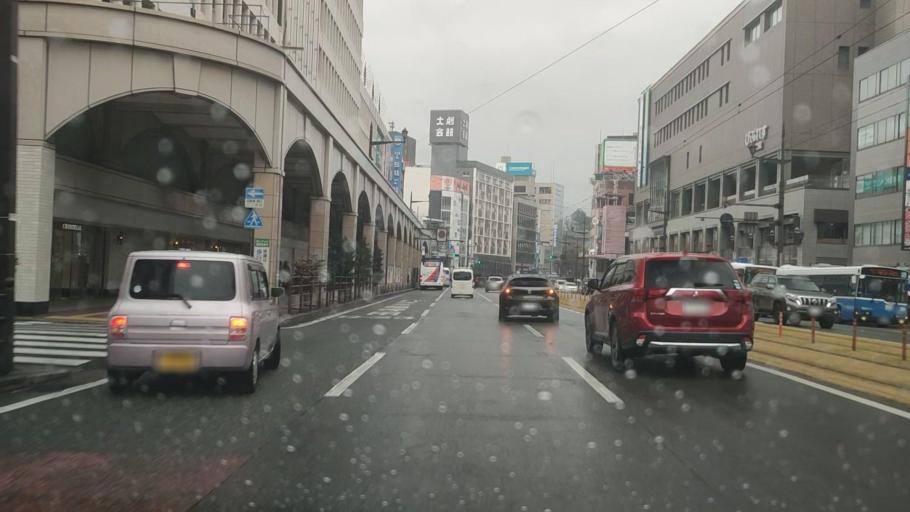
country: JP
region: Kumamoto
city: Kumamoto
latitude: 32.8025
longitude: 130.7120
